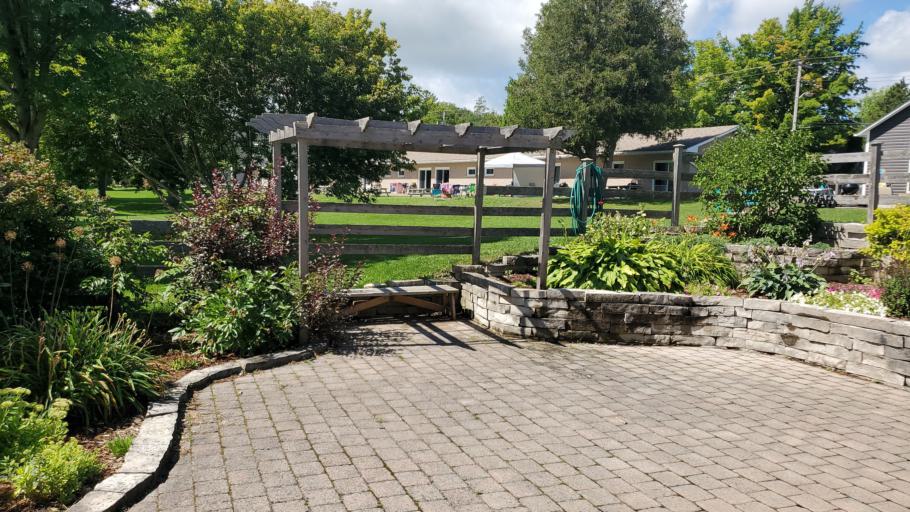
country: CA
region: Ontario
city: Tobermory
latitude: 44.9902
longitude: -81.2519
